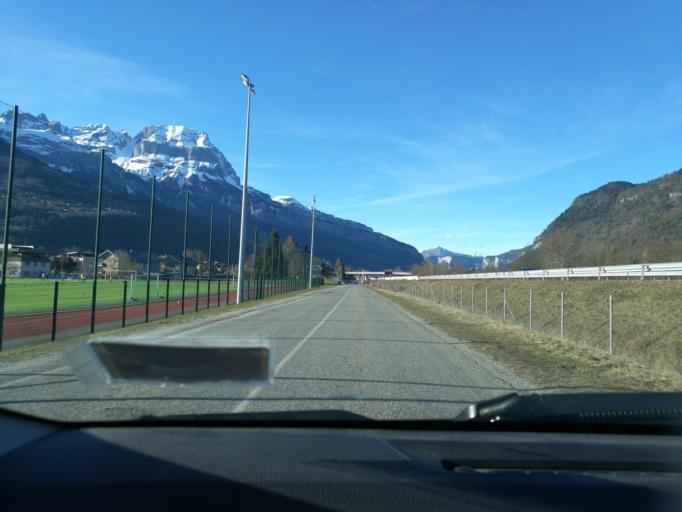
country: FR
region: Rhone-Alpes
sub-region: Departement de la Haute-Savoie
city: Sallanches
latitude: 45.9341
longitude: 6.6449
